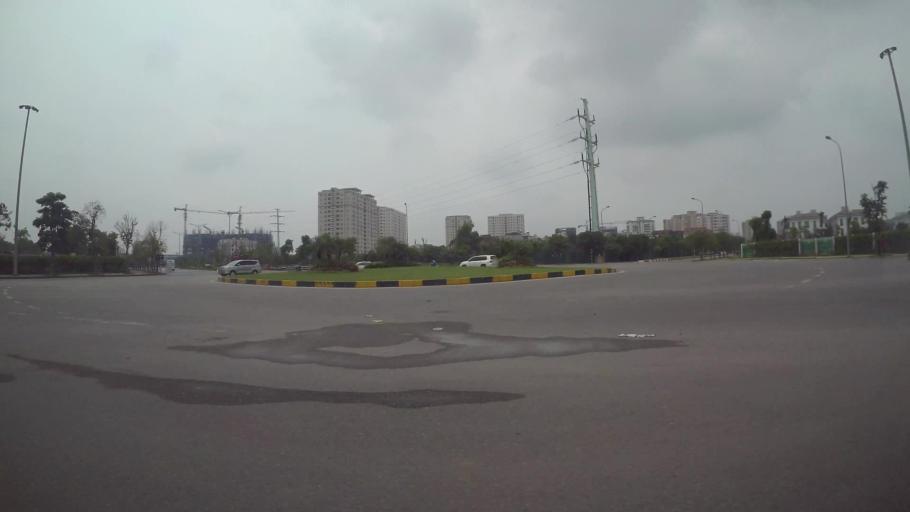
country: VN
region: Ha Noi
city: Trau Quy
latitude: 21.0431
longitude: 105.9126
